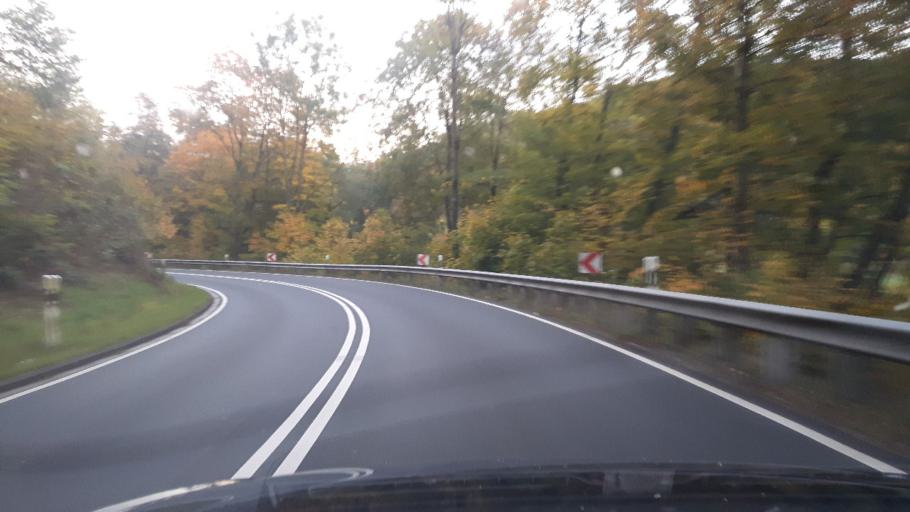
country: DE
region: North Rhine-Westphalia
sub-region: Regierungsbezirk Arnsberg
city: Bad Laasphe
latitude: 50.9387
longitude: 8.3777
